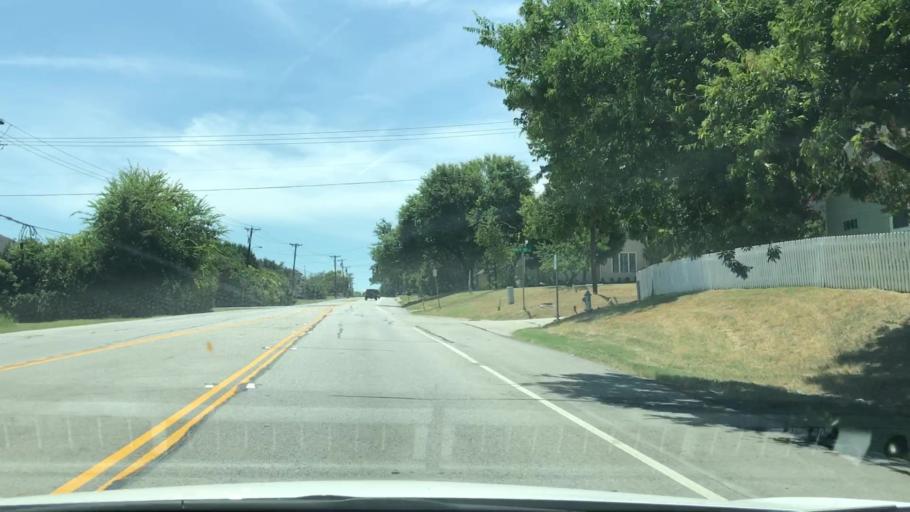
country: US
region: Texas
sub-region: Rockwall County
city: Rockwall
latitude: 32.9401
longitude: -96.4601
